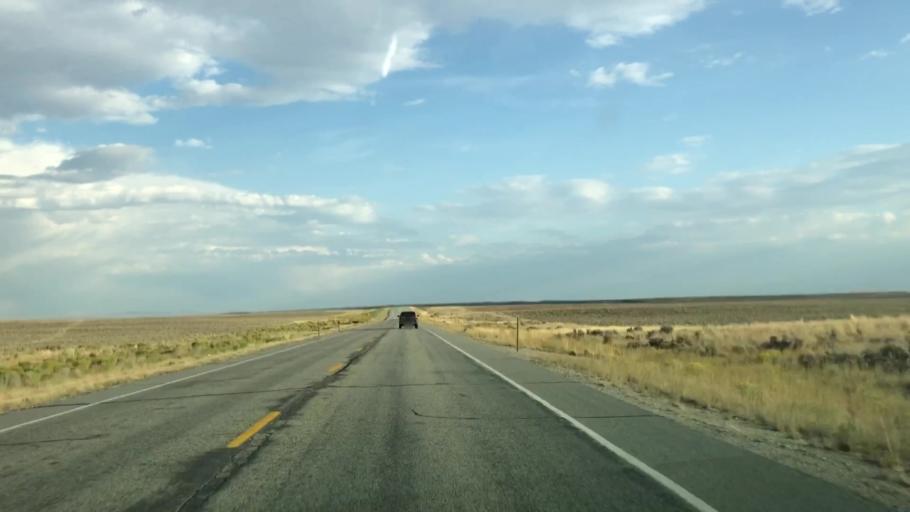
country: US
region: Wyoming
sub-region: Sublette County
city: Marbleton
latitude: 42.3251
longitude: -109.5119
